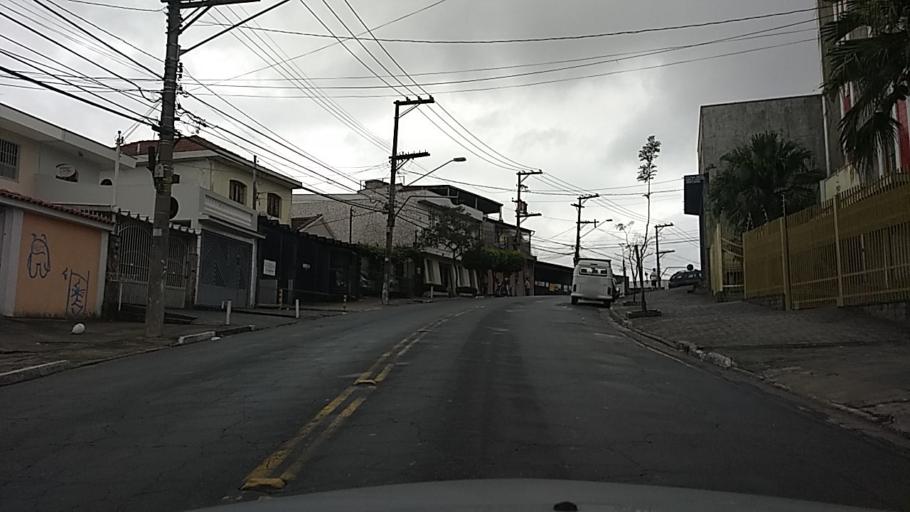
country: BR
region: Sao Paulo
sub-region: Guarulhos
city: Guarulhos
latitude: -23.4995
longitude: -46.5879
